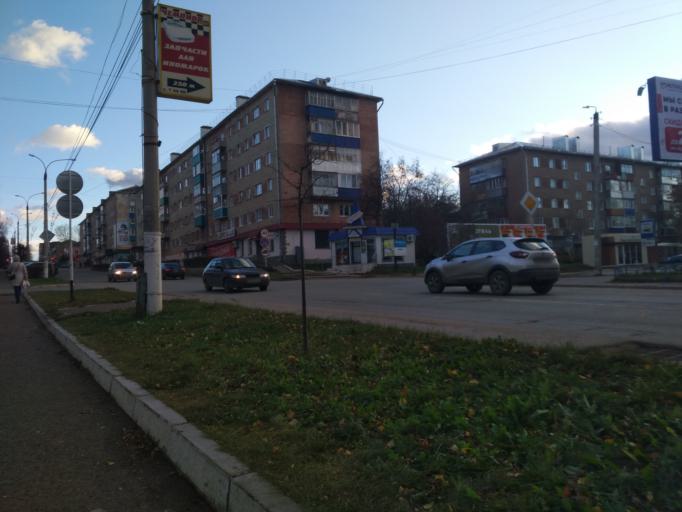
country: RU
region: Kirov
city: Vyatskiye Polyany
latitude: 56.2278
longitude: 51.0721
